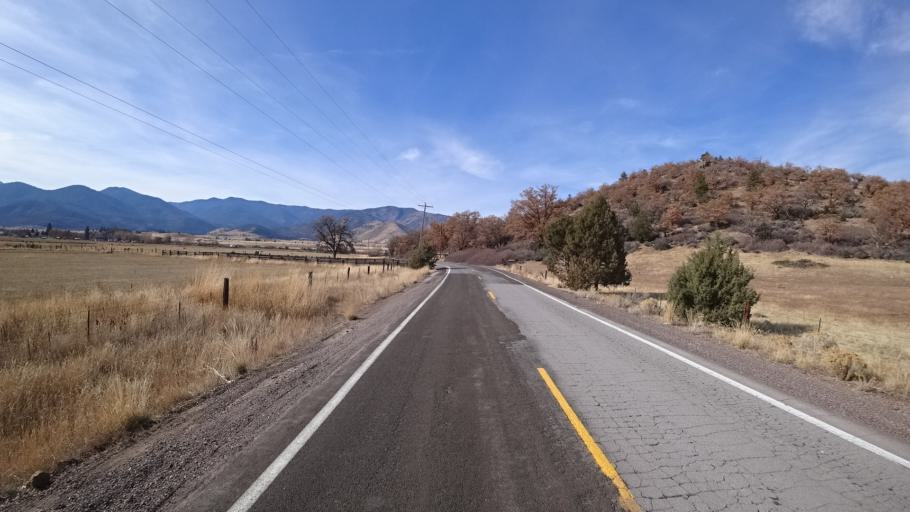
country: US
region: California
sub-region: Siskiyou County
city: Weed
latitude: 41.4677
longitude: -122.4245
